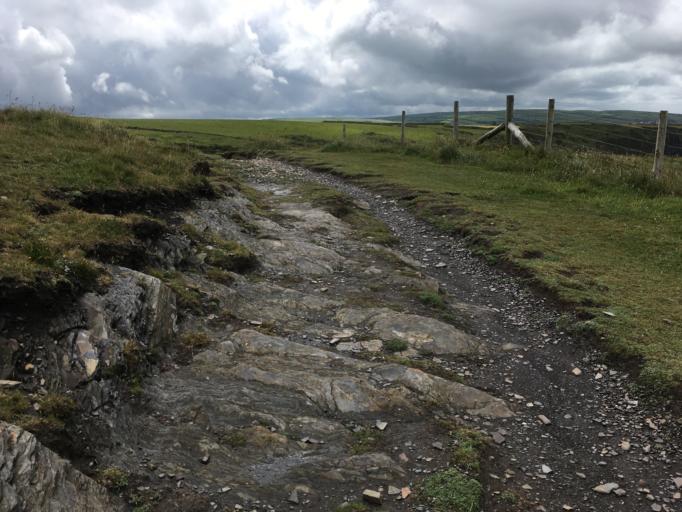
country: GB
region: England
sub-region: Cornwall
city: Camelford
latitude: 50.7089
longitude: -4.6643
